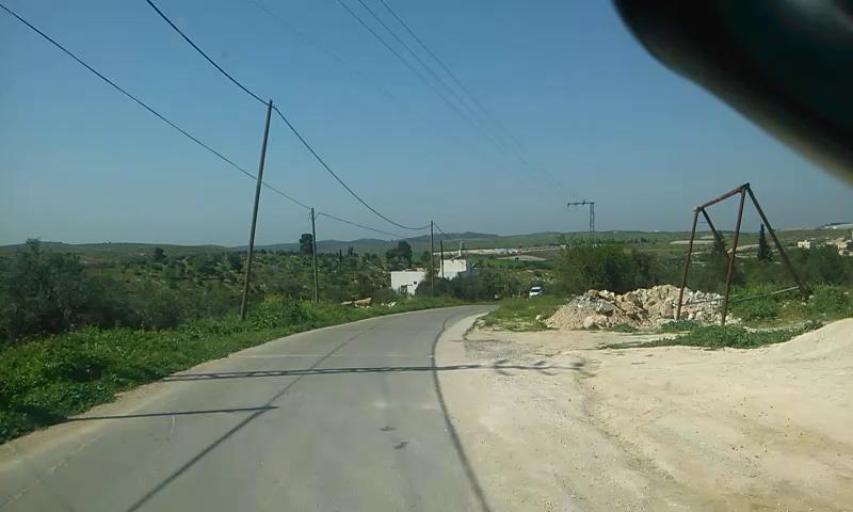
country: PS
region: West Bank
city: Al Majd
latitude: 31.4846
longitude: 34.9448
